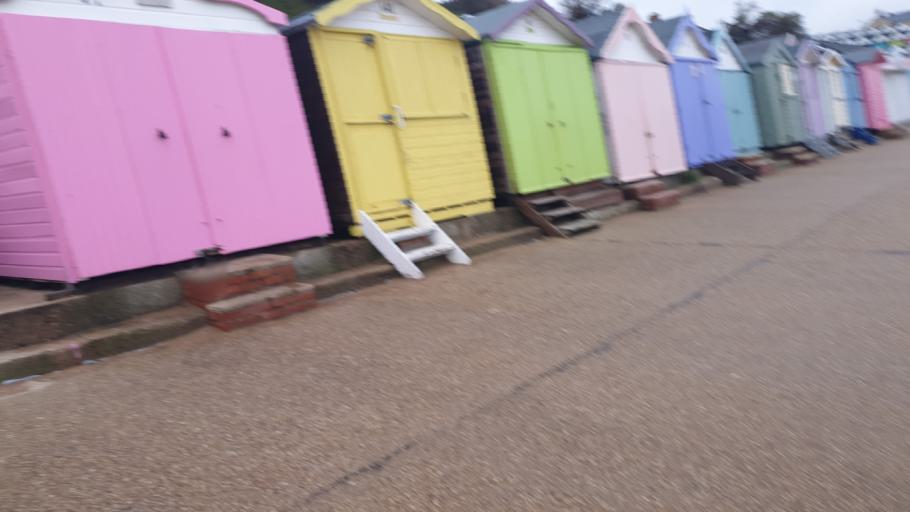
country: GB
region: England
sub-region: Essex
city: Walton-on-the-Naze
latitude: 51.8451
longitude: 1.2690
